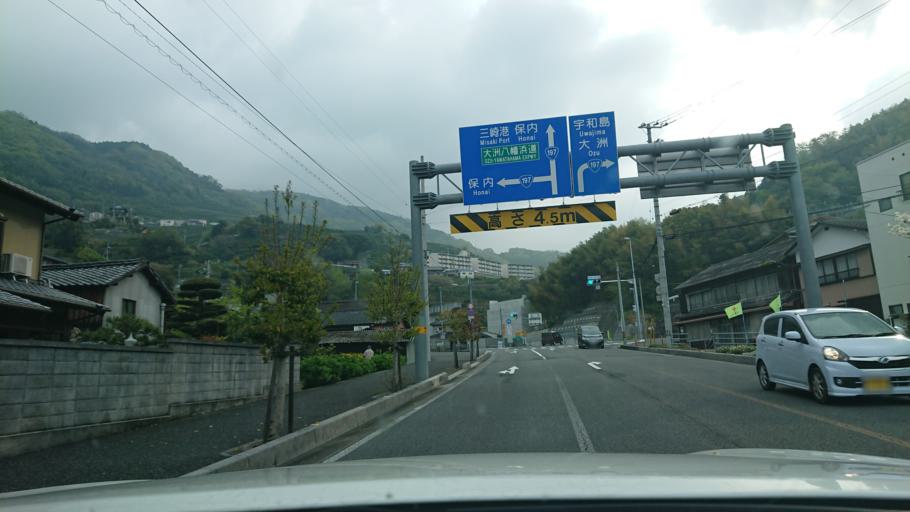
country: JP
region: Ehime
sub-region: Nishiuwa-gun
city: Ikata-cho
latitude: 33.4672
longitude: 132.4279
